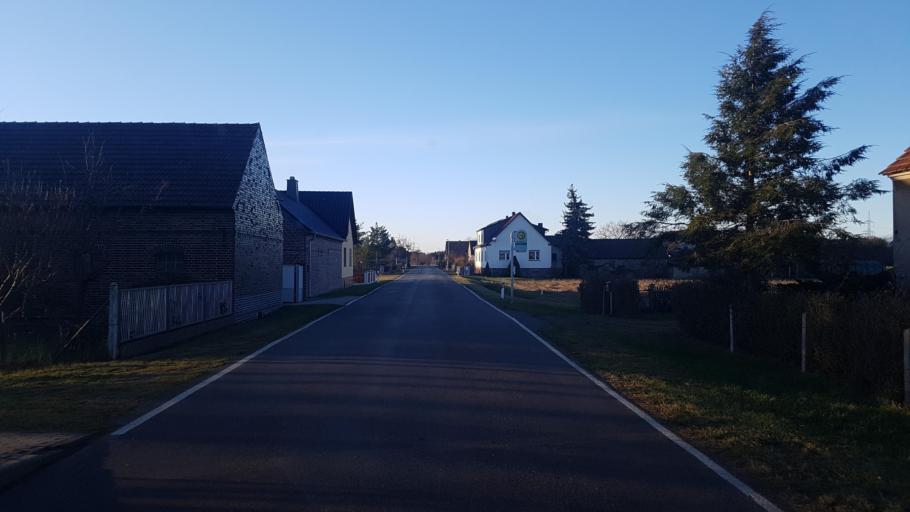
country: DE
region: Brandenburg
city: Drehnow
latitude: 51.8680
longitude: 14.3447
